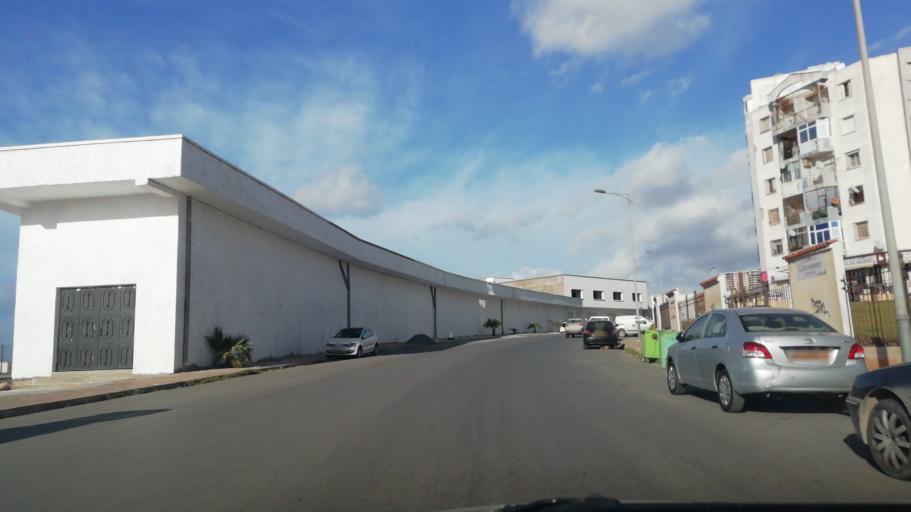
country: DZ
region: Oran
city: Bir el Djir
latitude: 35.7212
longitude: -0.5956
